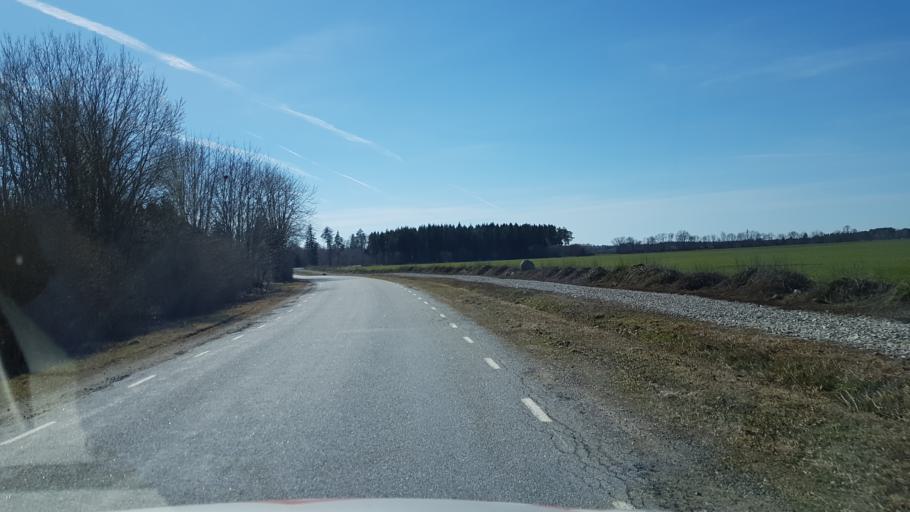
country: EE
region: Laeaene-Virumaa
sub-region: Viru-Nigula vald
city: Kunda
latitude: 59.3405
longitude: 26.6665
